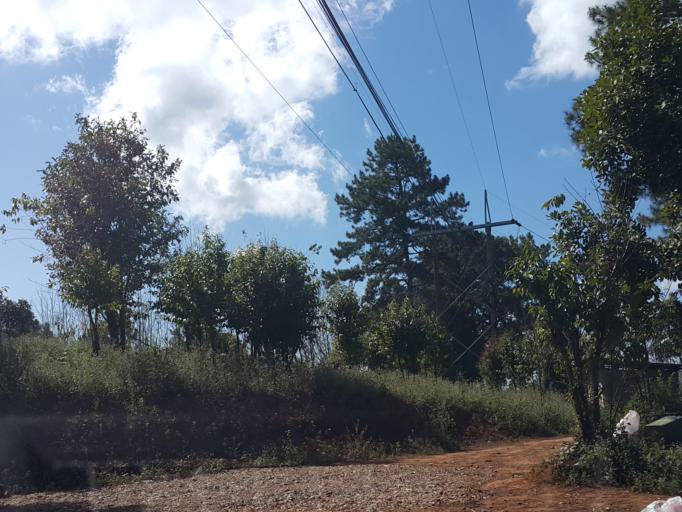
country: TH
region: Chiang Mai
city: Wiang Haeng
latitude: 19.5182
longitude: 98.7569
